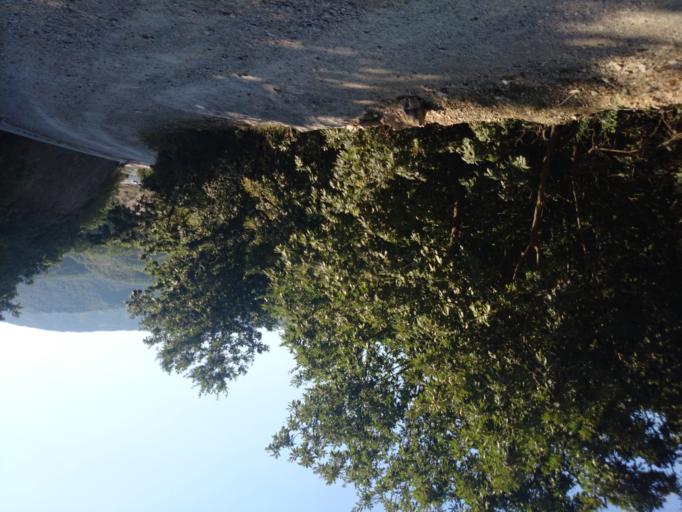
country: AL
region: Diber
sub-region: Rrethi i Bulqizes
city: Zerqan
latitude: 41.5154
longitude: 20.3889
